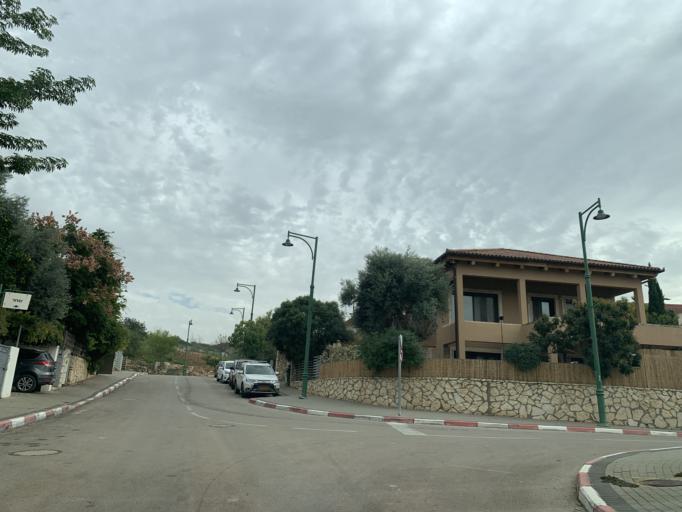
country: IL
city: Nirit
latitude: 32.1491
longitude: 34.9864
